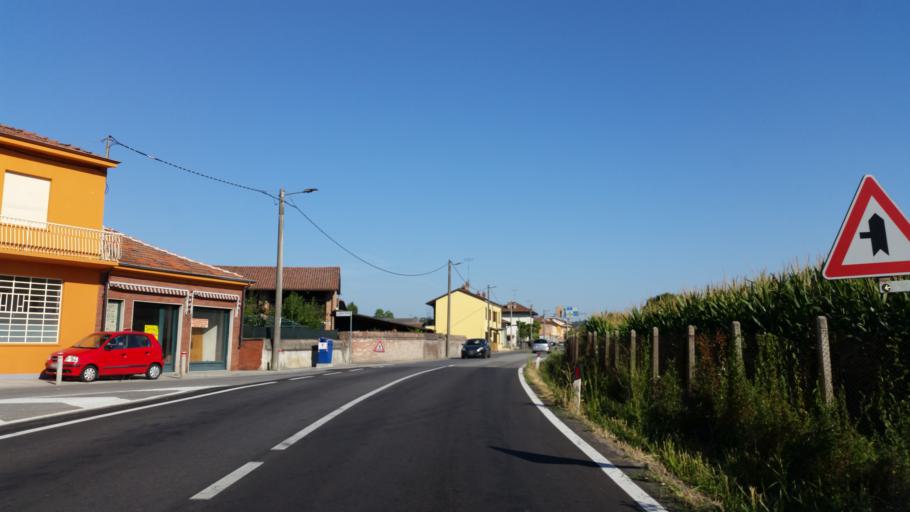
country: IT
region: Piedmont
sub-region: Provincia di Cuneo
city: Cinzano
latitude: 44.6850
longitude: 7.8976
